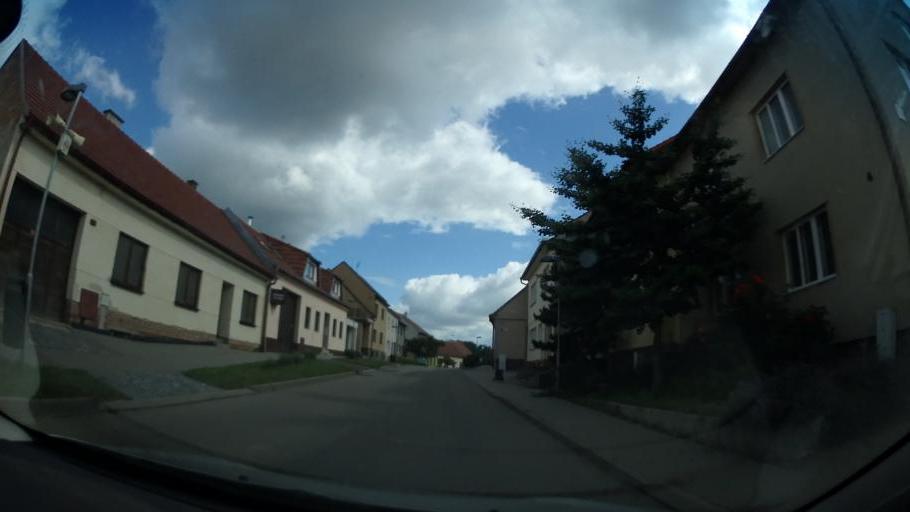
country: CZ
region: South Moravian
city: Orechov
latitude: 49.1124
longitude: 16.5172
